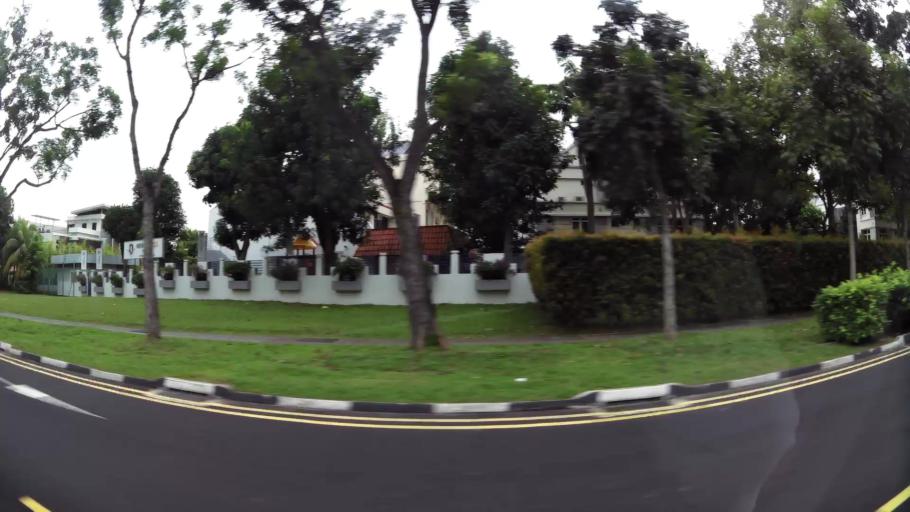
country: SG
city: Singapore
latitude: 1.3691
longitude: 103.8805
